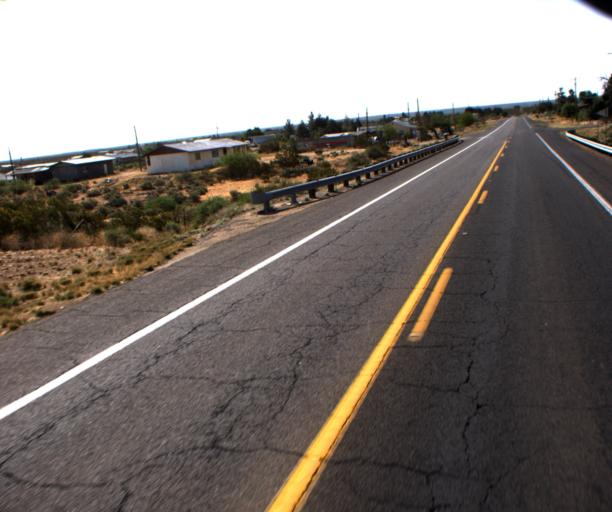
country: US
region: Arizona
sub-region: Graham County
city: Swift Trail Junction
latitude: 32.7264
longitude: -109.7127
